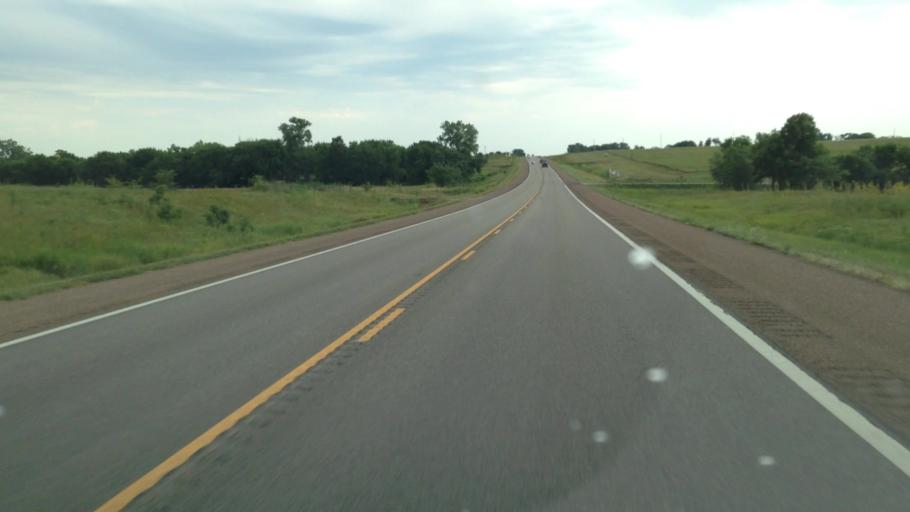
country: US
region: Kansas
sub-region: Woodson County
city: Yates Center
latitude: 38.0143
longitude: -95.7392
